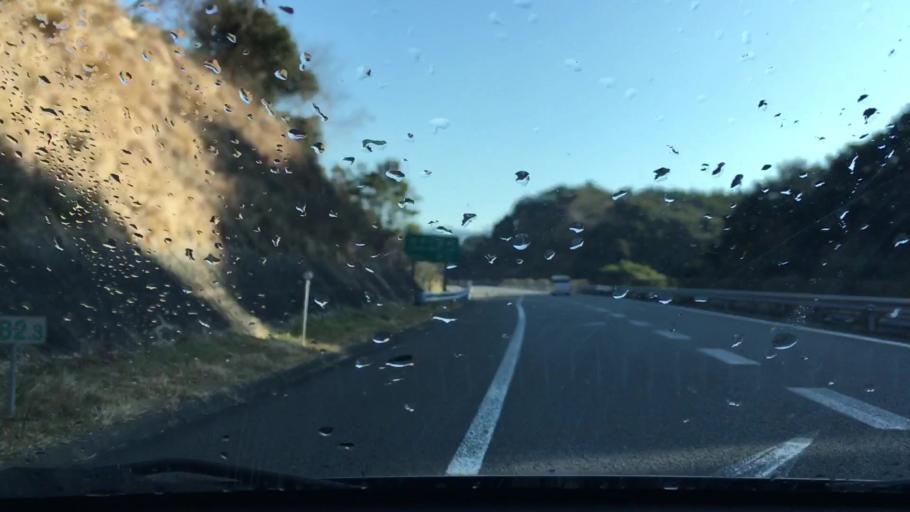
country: JP
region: Kagoshima
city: Kokubu-matsuki
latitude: 31.7436
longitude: 130.8042
